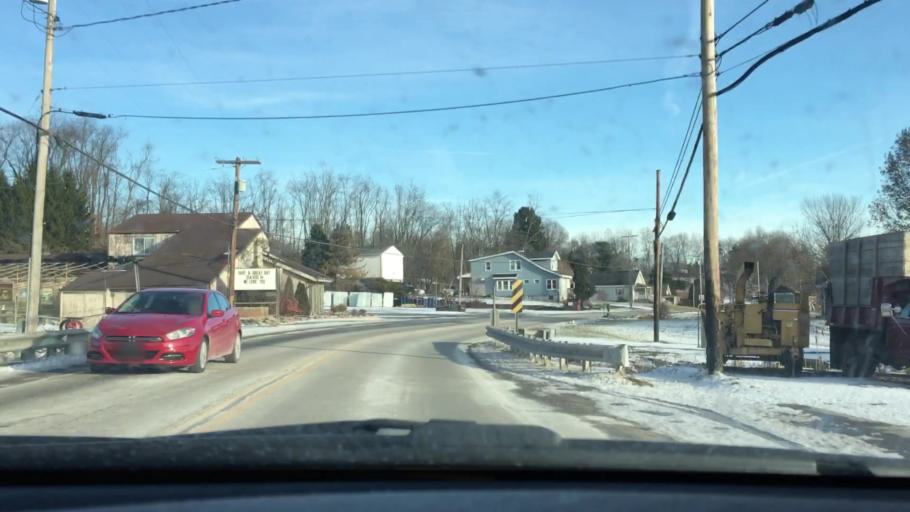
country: US
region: Pennsylvania
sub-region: Washington County
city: Gastonville
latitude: 40.2696
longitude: -80.0129
